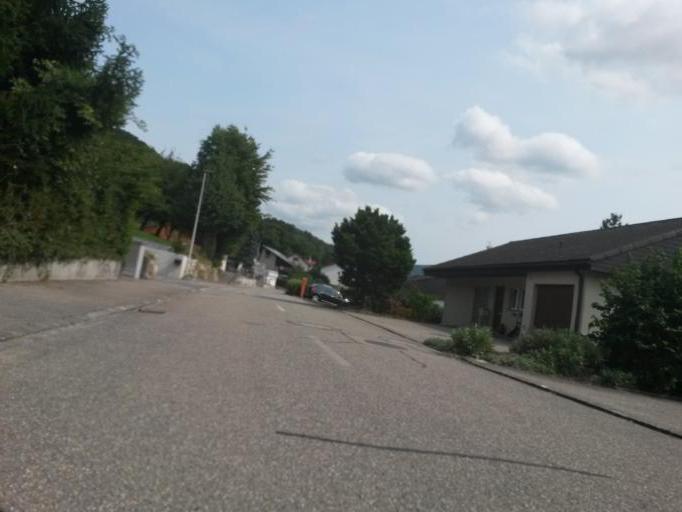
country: CH
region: Solothurn
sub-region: Bezirk Thal
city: Laupersdorf
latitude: 47.3130
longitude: 7.6602
